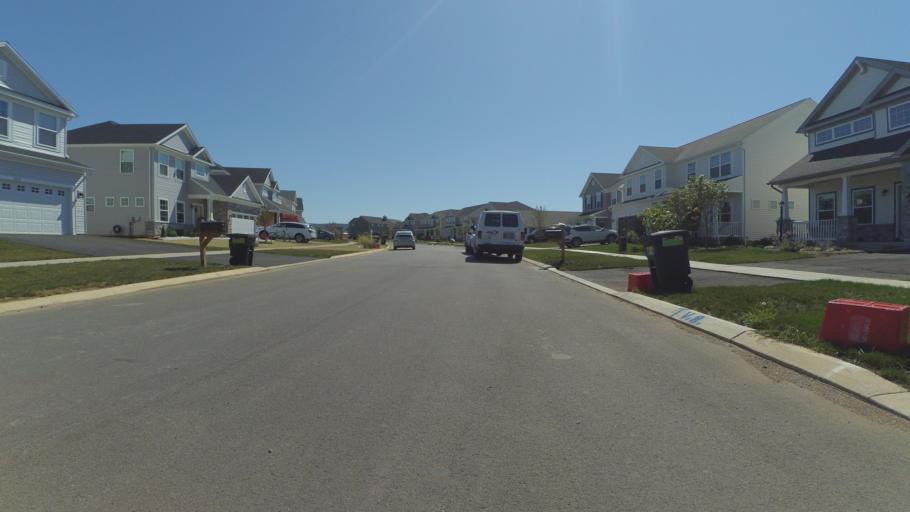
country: US
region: Pennsylvania
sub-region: Centre County
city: Pine Grove Mills
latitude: 40.7699
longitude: -77.8990
